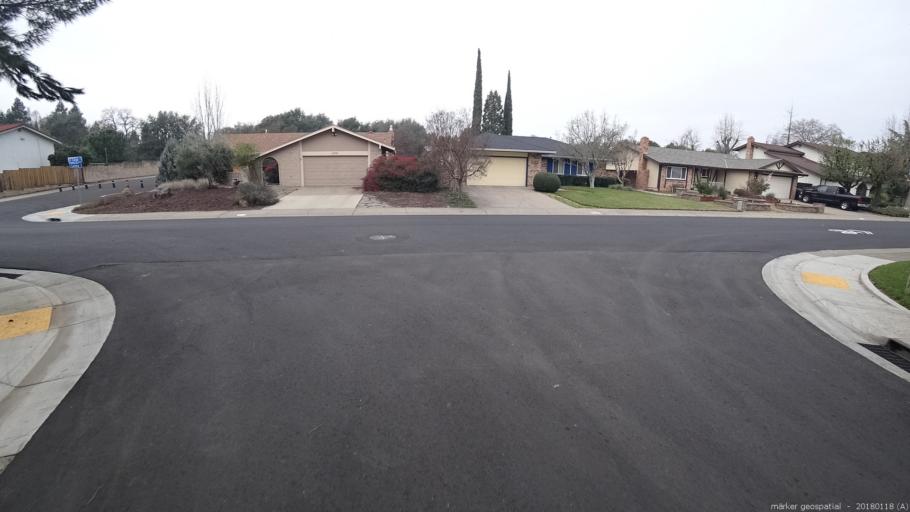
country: US
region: California
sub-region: Sacramento County
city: Rancho Cordova
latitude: 38.5889
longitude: -121.3231
